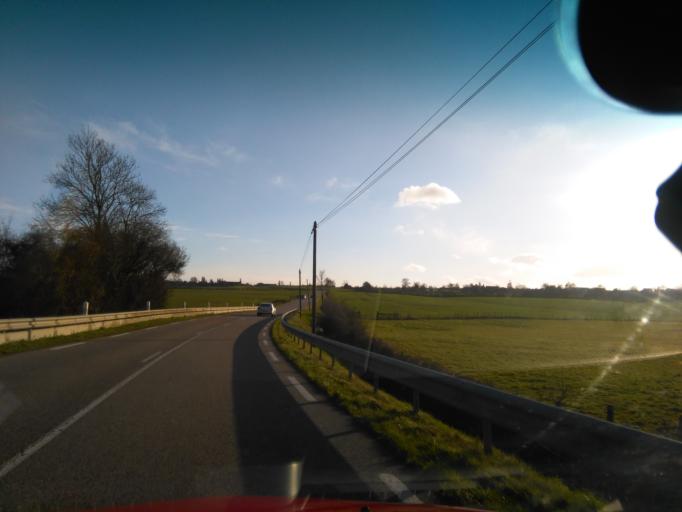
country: FR
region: Lower Normandy
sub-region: Departement de l'Orne
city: Courteilles
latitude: 48.8320
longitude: -0.2366
